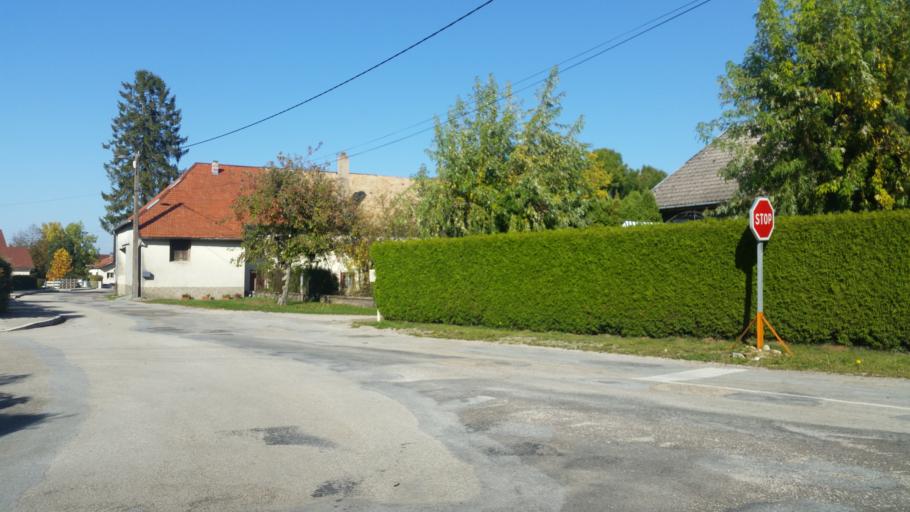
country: FR
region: Franche-Comte
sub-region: Departement du Doubs
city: Levier
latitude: 47.0363
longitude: 6.0748
